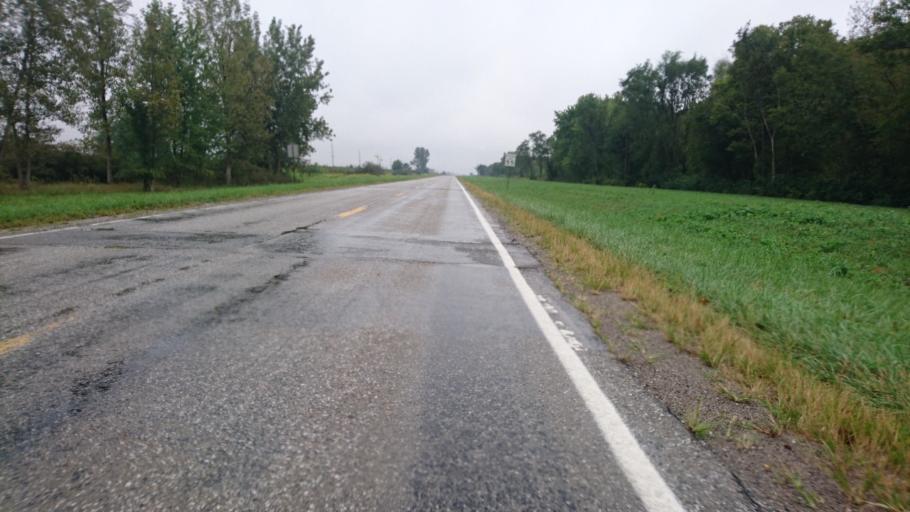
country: US
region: Illinois
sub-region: Sangamon County
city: Williamsville
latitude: 40.0178
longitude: -89.4872
